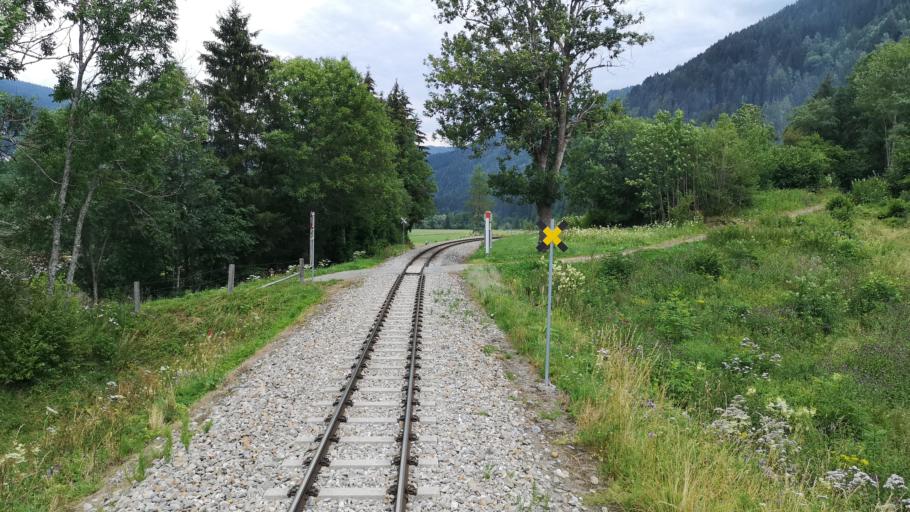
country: AT
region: Styria
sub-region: Politischer Bezirk Murau
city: St. Ruprecht-Falkendorf
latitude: 47.0890
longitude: 13.9938
